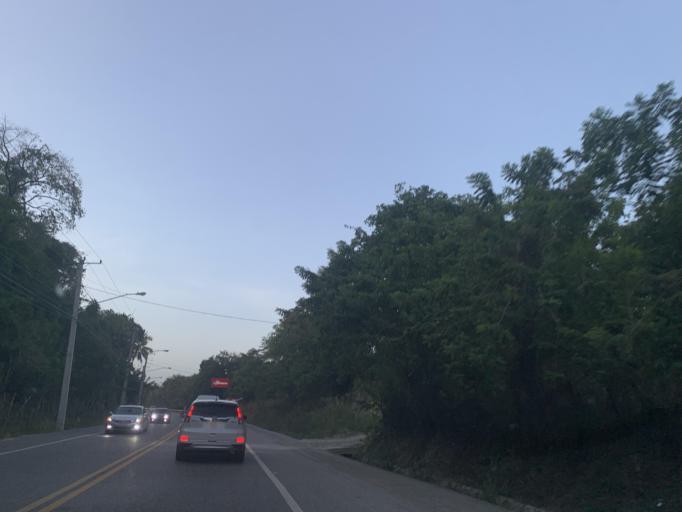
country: DO
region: Puerto Plata
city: Imbert
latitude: 19.8039
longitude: -70.7789
